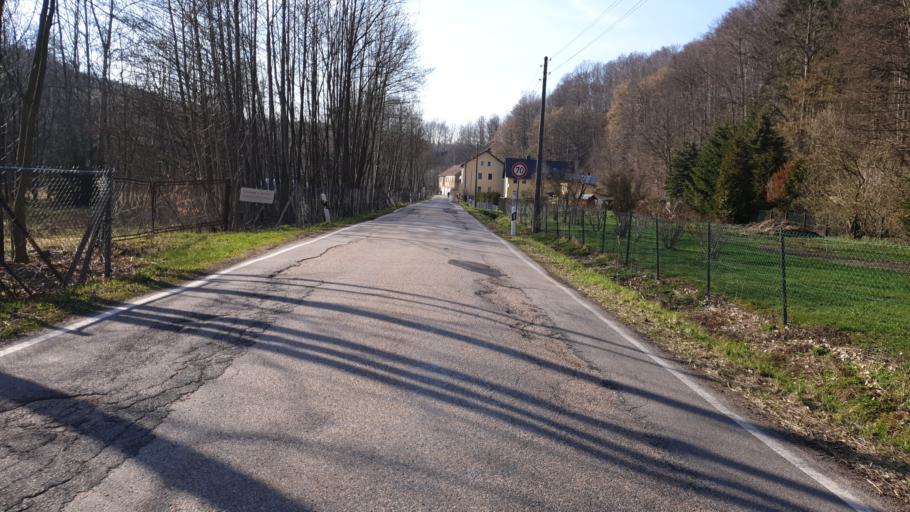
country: DE
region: Saxony
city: Burgstadt
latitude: 50.9445
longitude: 12.8177
